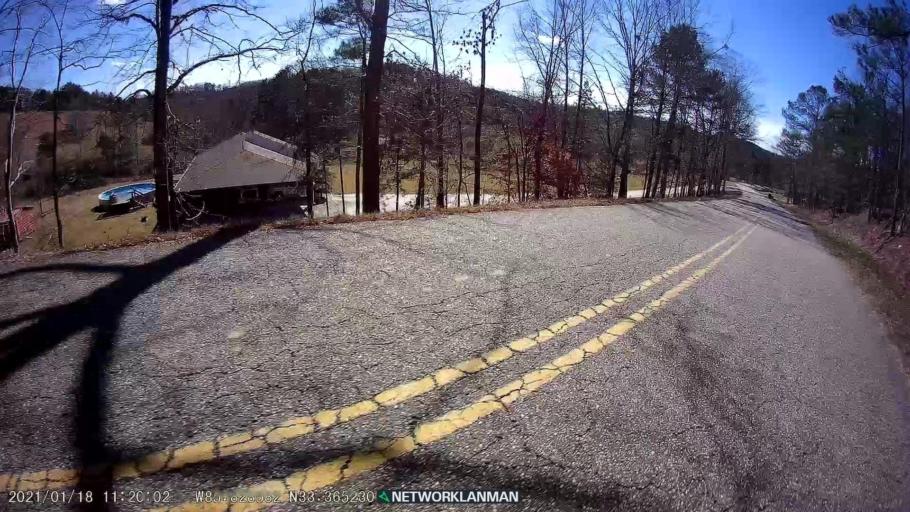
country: US
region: Alabama
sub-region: Clay County
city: Ashland
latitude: 33.3651
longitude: -85.8287
